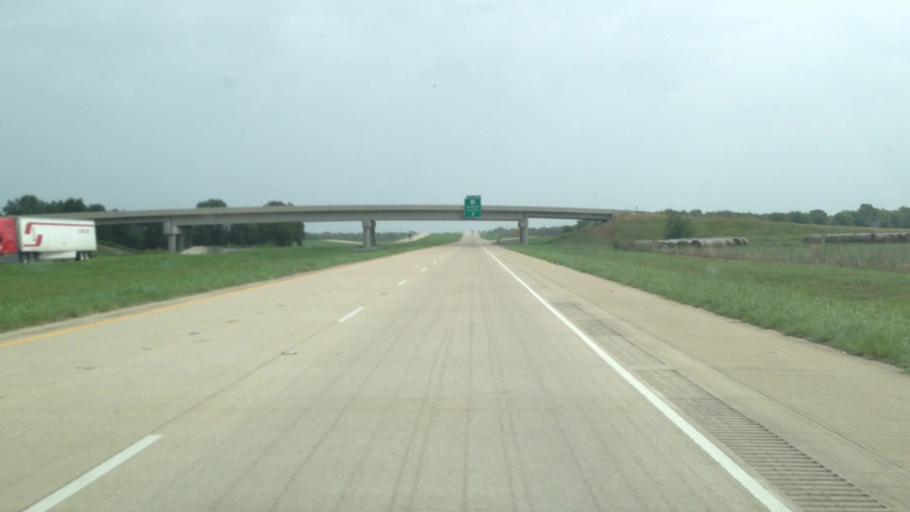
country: US
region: Louisiana
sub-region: Caddo Parish
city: Vivian
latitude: 32.8437
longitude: -93.8683
